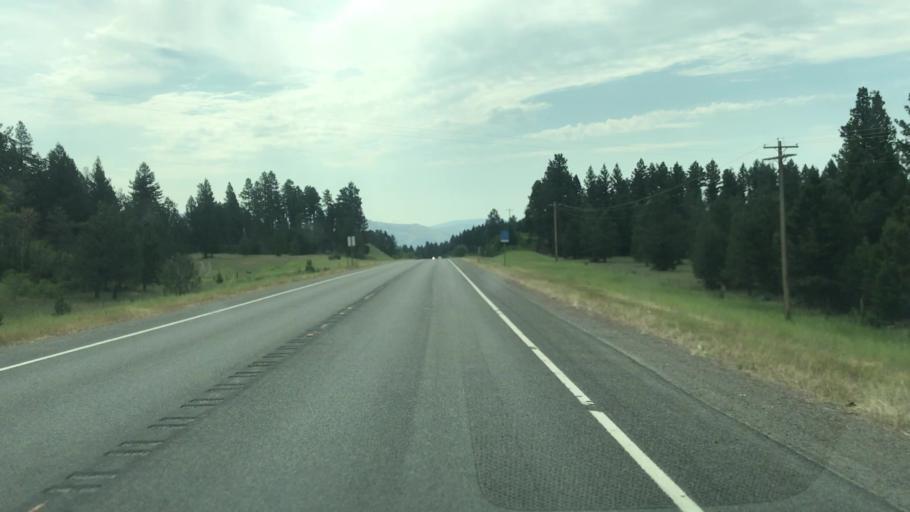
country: US
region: Montana
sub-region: Lewis and Clark County
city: Lincoln
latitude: 47.0133
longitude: -113.0667
